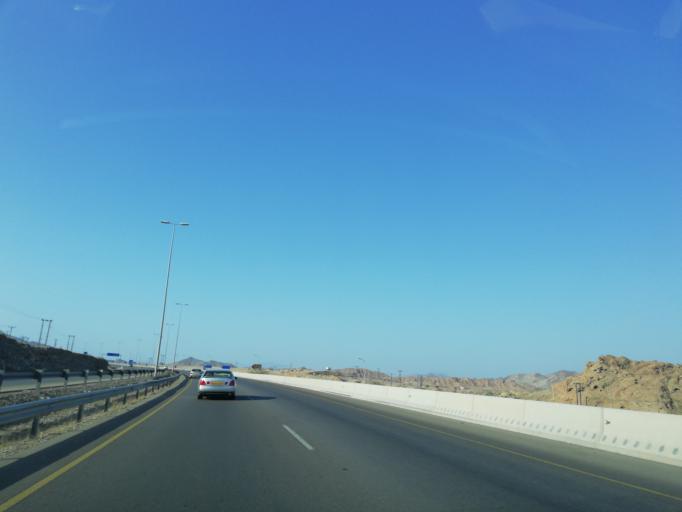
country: OM
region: Muhafazat ad Dakhiliyah
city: Bidbid
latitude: 23.4404
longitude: 58.1205
